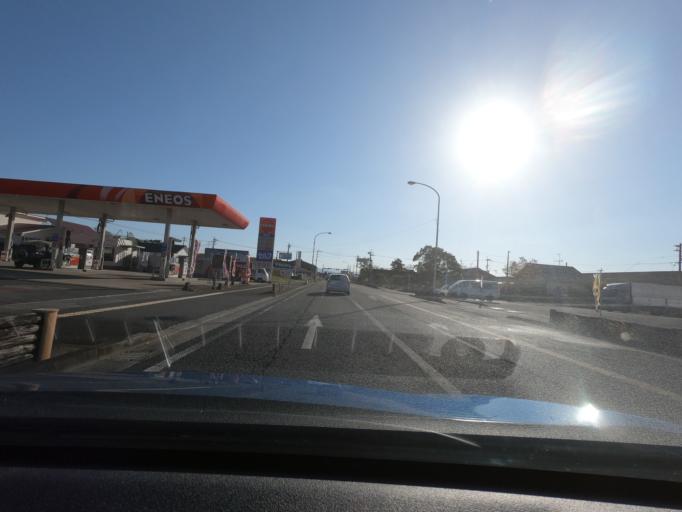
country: JP
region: Kagoshima
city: Izumi
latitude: 32.1251
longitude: 130.3427
